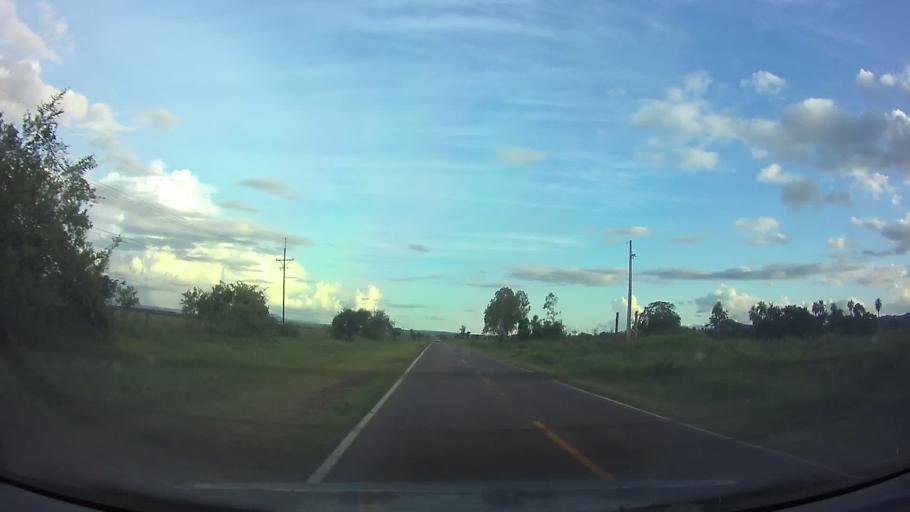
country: PY
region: Paraguari
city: Carapegua
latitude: -25.8194
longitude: -57.1708
